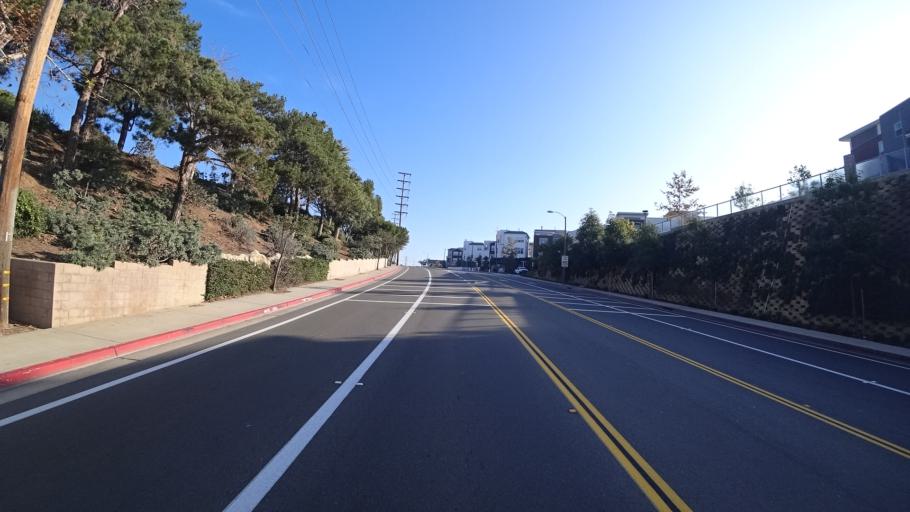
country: US
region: California
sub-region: Orange County
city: Costa Mesa
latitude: 33.6510
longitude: -117.9491
